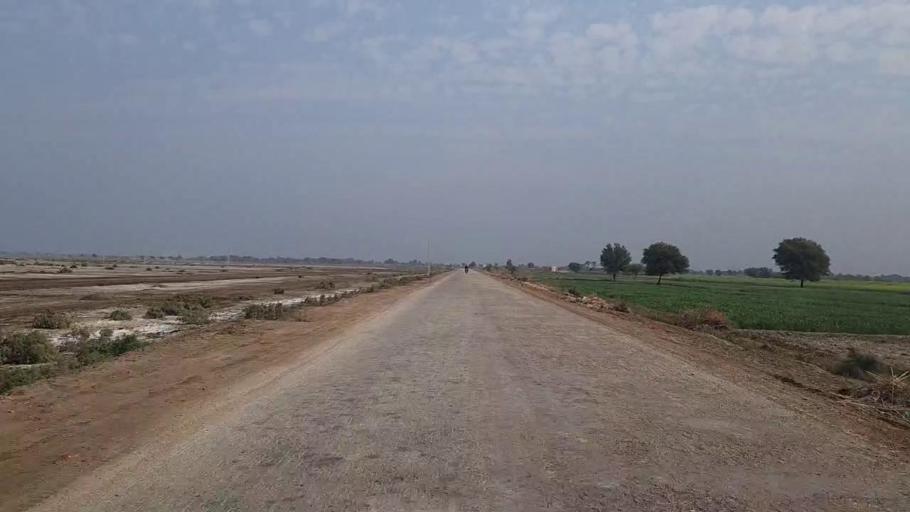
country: PK
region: Sindh
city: Mirwah Gorchani
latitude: 25.4076
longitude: 69.0438
